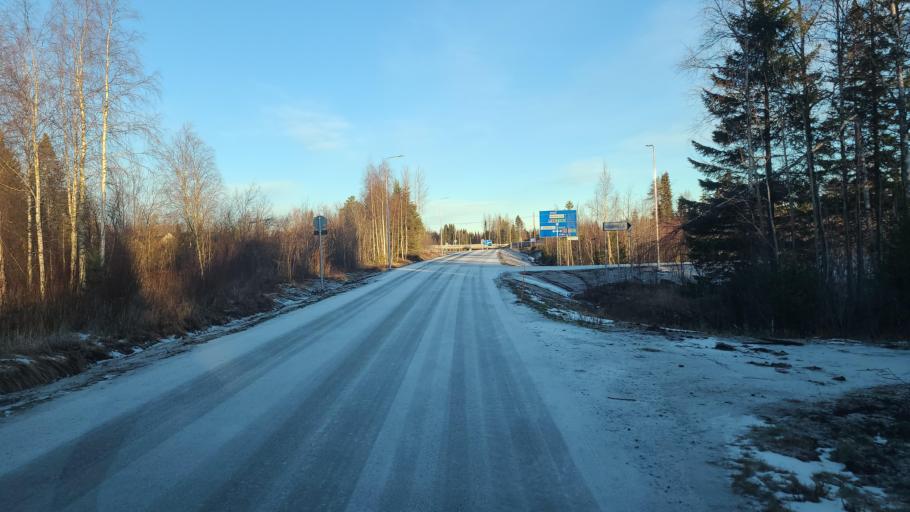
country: FI
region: Lapland
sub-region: Kemi-Tornio
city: Kemi
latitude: 65.6755
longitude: 24.7434
